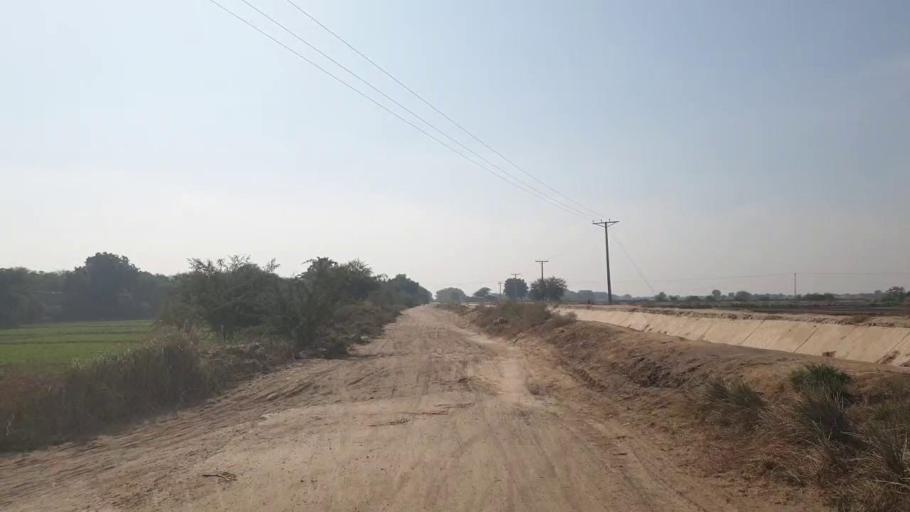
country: PK
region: Sindh
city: Matiari
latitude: 25.6644
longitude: 68.3451
